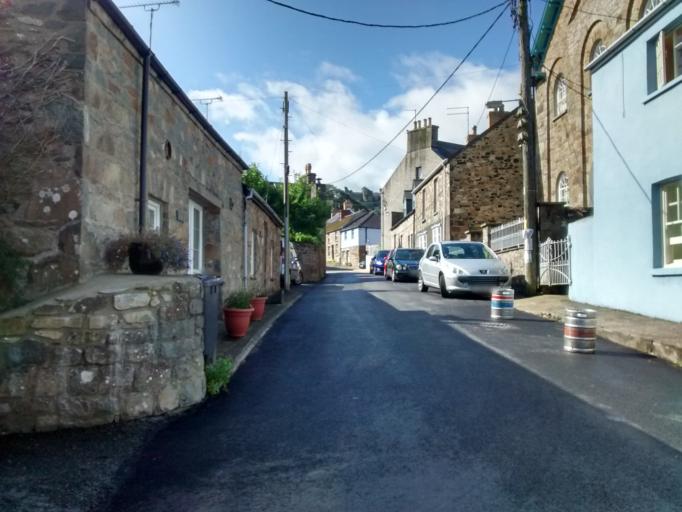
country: GB
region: Wales
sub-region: Pembrokeshire
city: Newport
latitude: 52.0171
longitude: -4.8310
